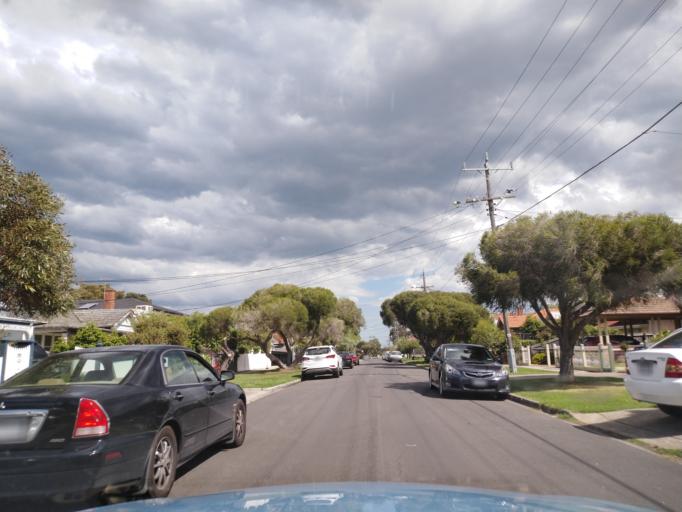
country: AU
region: Victoria
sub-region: Hobsons Bay
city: Newport
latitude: -37.8385
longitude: 144.8797
